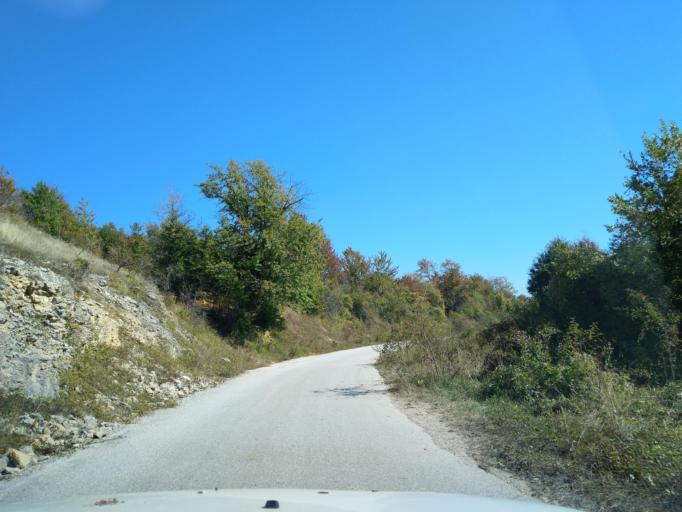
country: RS
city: Sokolovica
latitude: 43.2492
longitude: 20.3254
